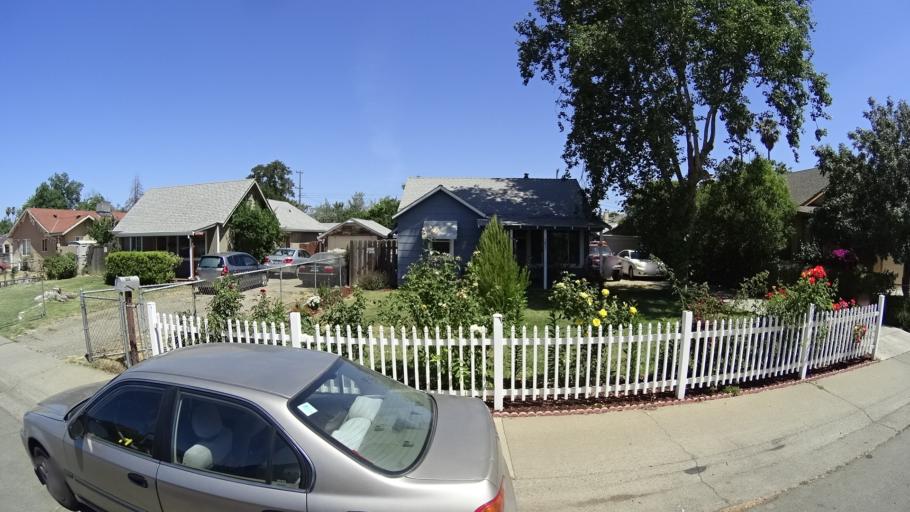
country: US
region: California
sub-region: Sacramento County
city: Parkway
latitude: 38.5182
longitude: -121.4742
